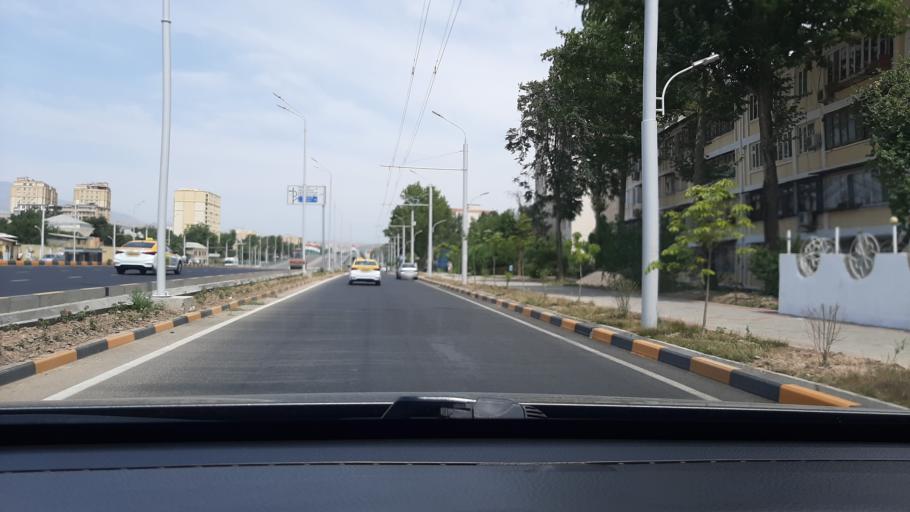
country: TJ
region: Dushanbe
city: Dushanbe
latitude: 38.5826
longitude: 68.7362
